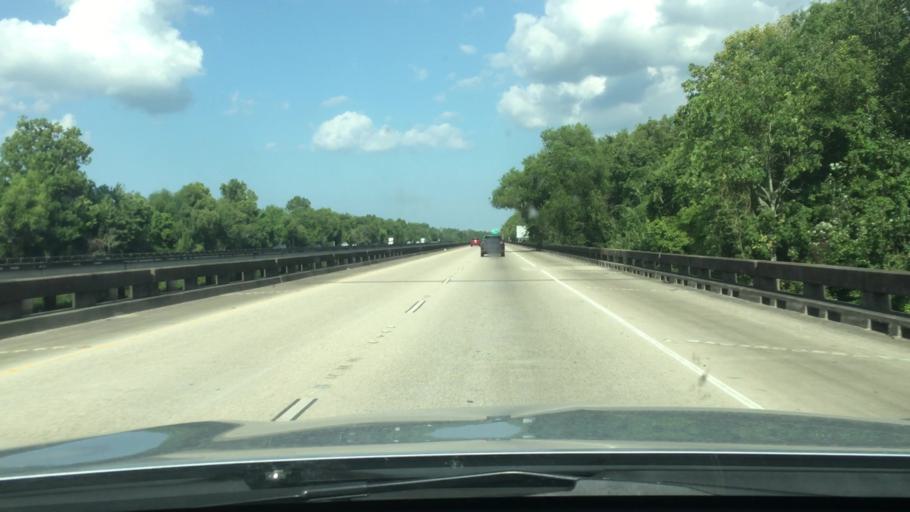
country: US
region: Louisiana
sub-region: Saint John the Baptist Parish
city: Montegut
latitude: 30.1082
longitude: -90.5186
